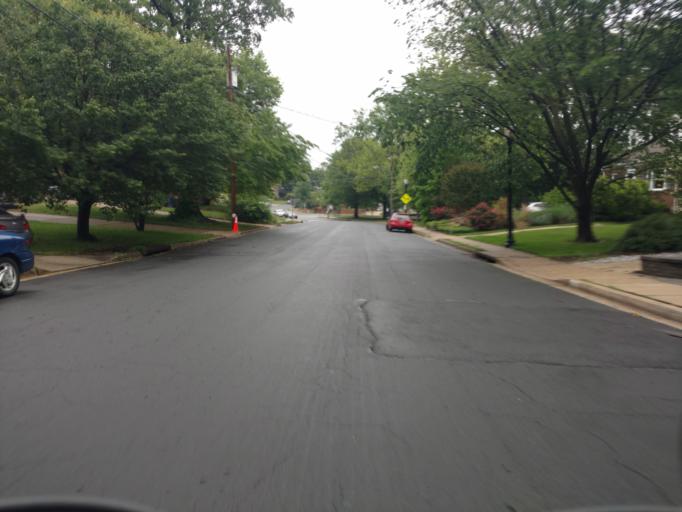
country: US
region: Virginia
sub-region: Arlington County
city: Arlington
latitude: 38.8675
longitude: -77.0831
